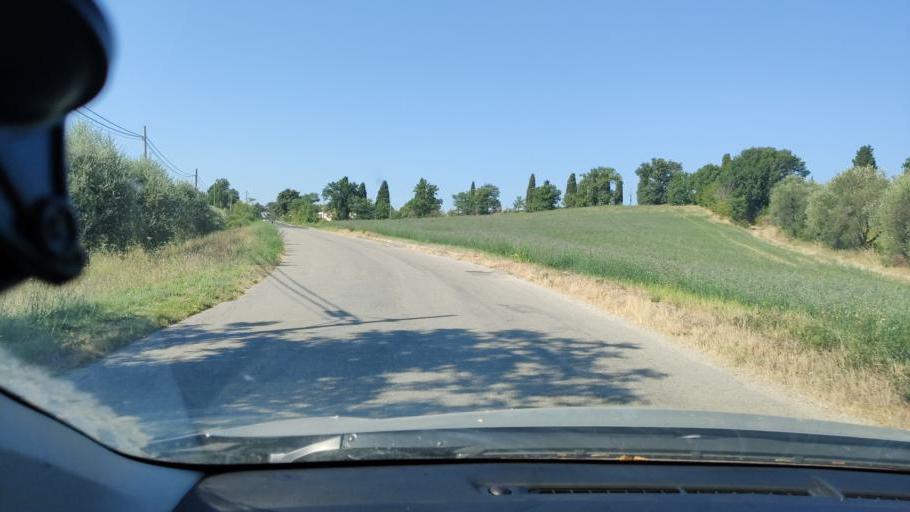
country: IT
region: Umbria
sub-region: Provincia di Terni
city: Fornole
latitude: 42.5248
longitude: 12.4350
